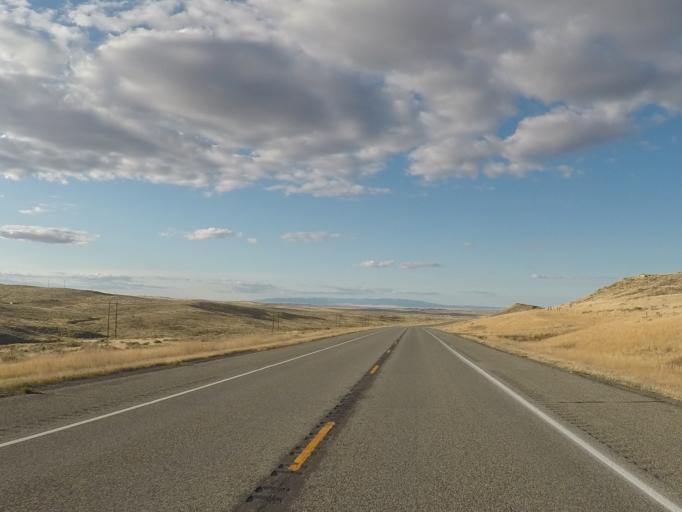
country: US
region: Montana
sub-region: Golden Valley County
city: Ryegate
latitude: 46.1480
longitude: -108.8940
